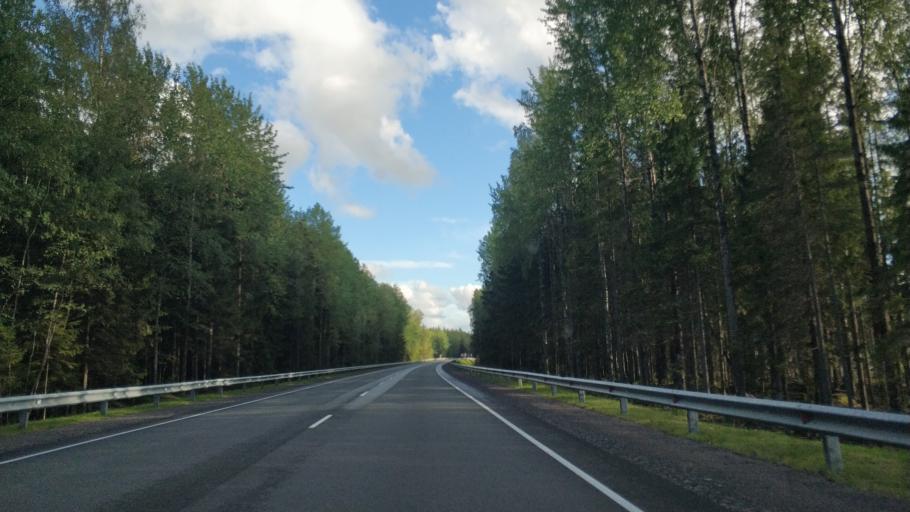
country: RU
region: Leningrad
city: Priozersk
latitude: 60.9125
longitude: 30.1577
